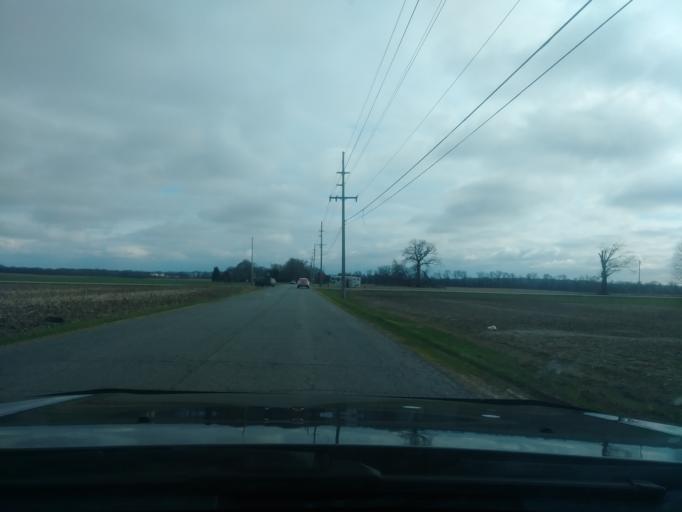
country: US
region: Indiana
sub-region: LaPorte County
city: LaPorte
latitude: 41.6115
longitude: -86.7972
